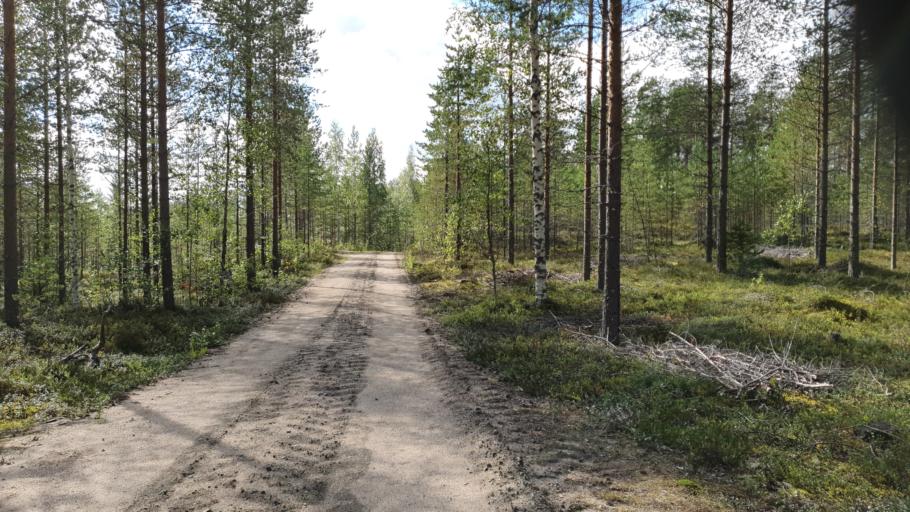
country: FI
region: Kainuu
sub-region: Kehys-Kainuu
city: Kuhmo
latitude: 64.1486
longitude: 29.3569
